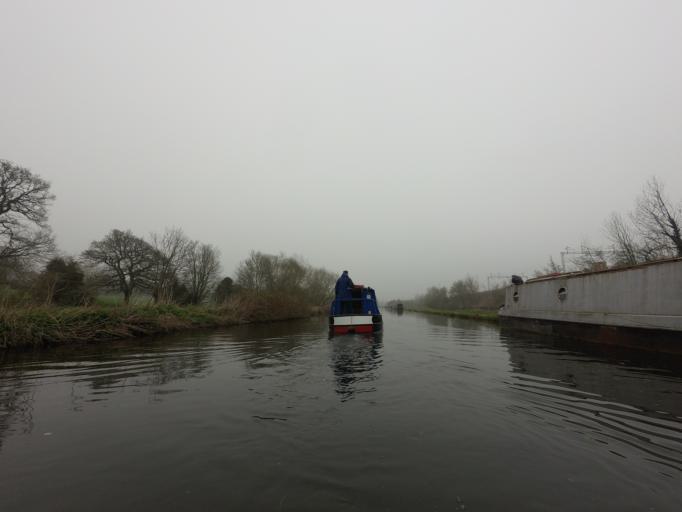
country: GB
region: England
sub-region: Hertfordshire
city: Hemel Hempstead
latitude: 51.7458
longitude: -0.5048
